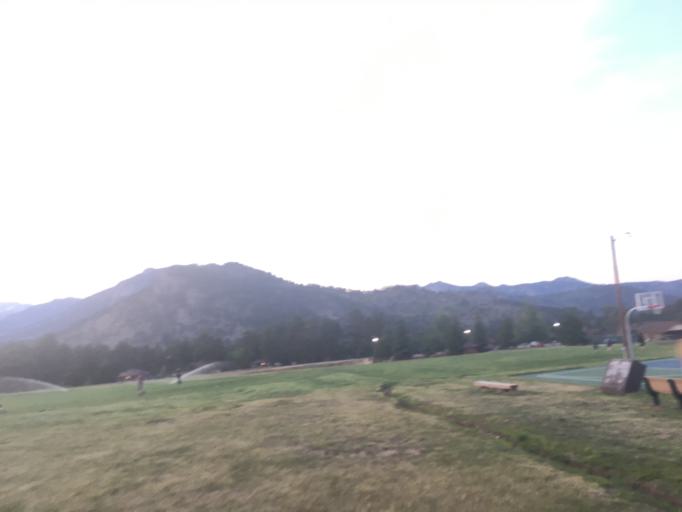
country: US
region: Colorado
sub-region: Larimer County
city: Estes Park
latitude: 40.3409
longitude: -105.5725
